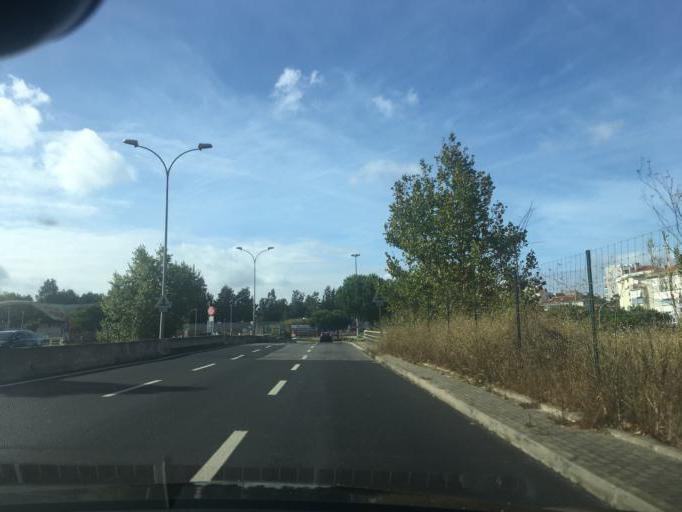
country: PT
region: Lisbon
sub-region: Odivelas
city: Odivelas
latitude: 38.7831
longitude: -9.1908
